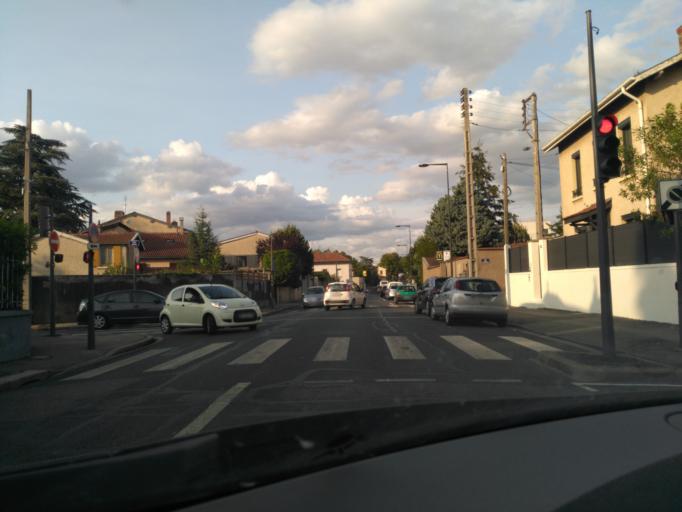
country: FR
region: Rhone-Alpes
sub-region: Departement du Rhone
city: Caluire-et-Cuire
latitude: 45.7895
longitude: 4.8356
